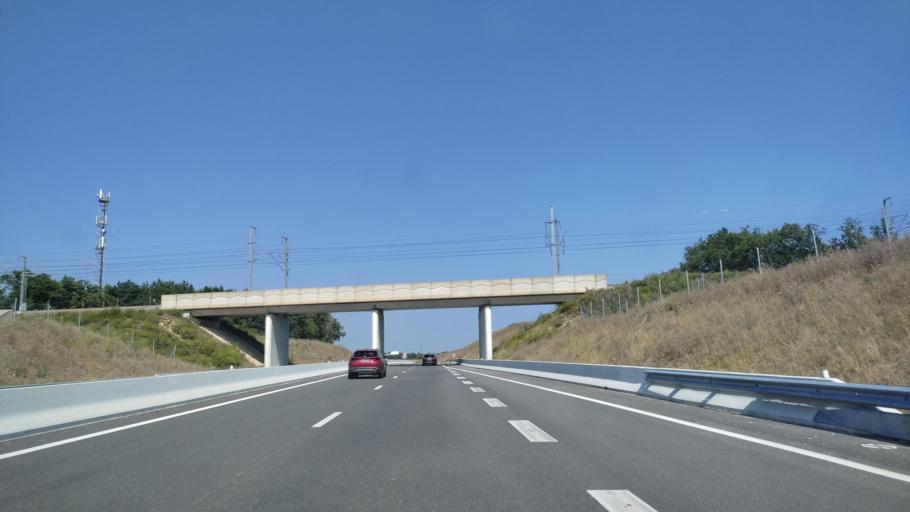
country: FR
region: Poitou-Charentes
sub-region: Departement de la Charente
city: Saint-Saturnin
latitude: 45.6826
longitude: 0.0727
